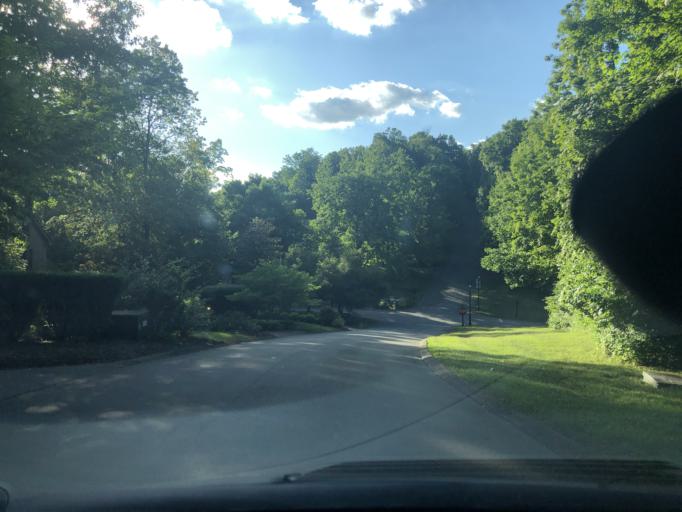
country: US
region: Tennessee
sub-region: Davidson County
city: Forest Hills
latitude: 36.0521
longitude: -86.8308
